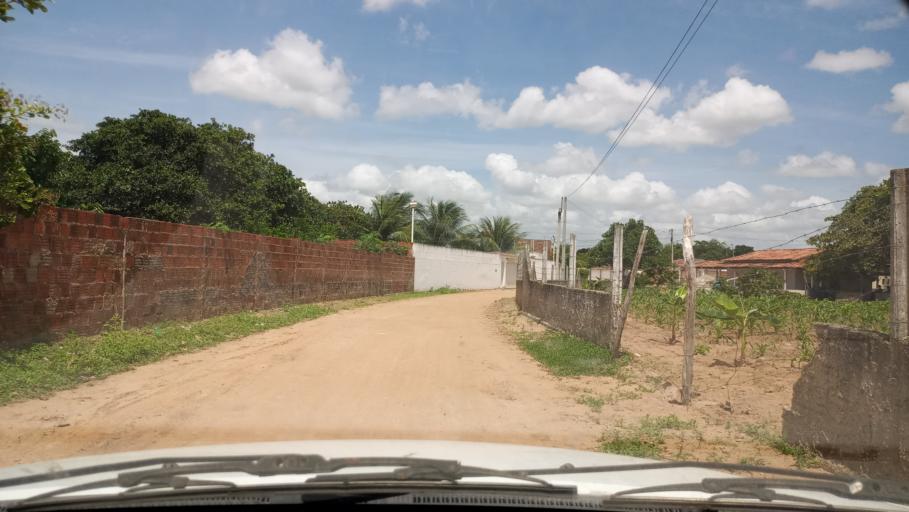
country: BR
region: Rio Grande do Norte
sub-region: Brejinho
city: Brejinho
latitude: -6.2632
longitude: -35.3707
